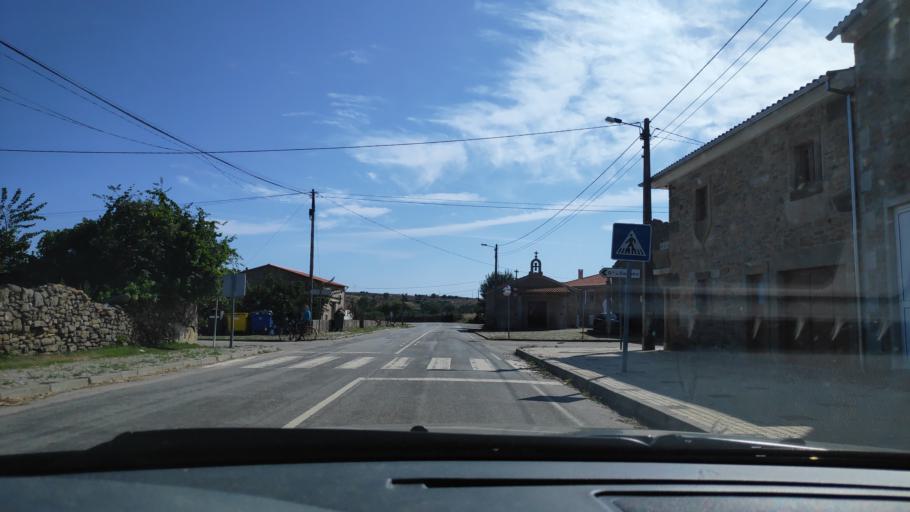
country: PT
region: Braganca
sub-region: Miranda do Douro
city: Miranda do Douro
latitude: 41.4729
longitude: -6.3551
